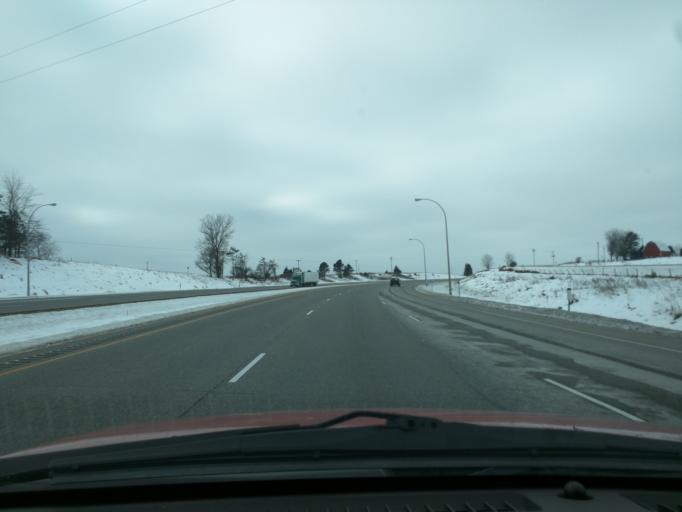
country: US
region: Wisconsin
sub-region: Trempealeau County
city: Trempealeau
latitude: 43.9244
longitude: -91.4410
